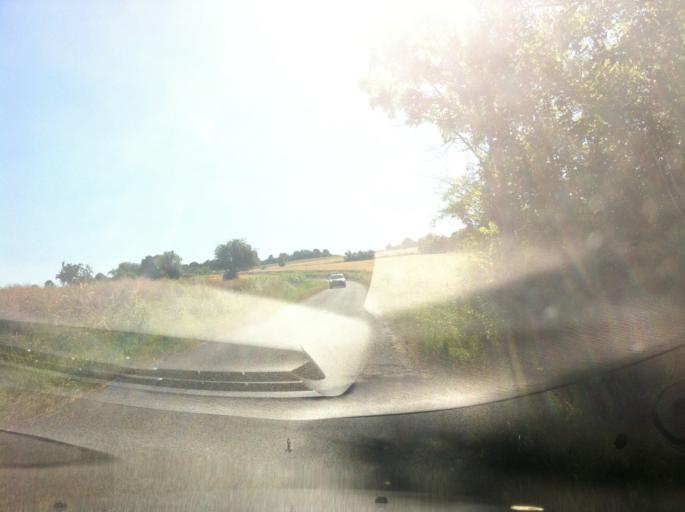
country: FR
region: Auvergne
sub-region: Departement de l'Allier
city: Chantelle
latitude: 46.1952
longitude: 3.1627
